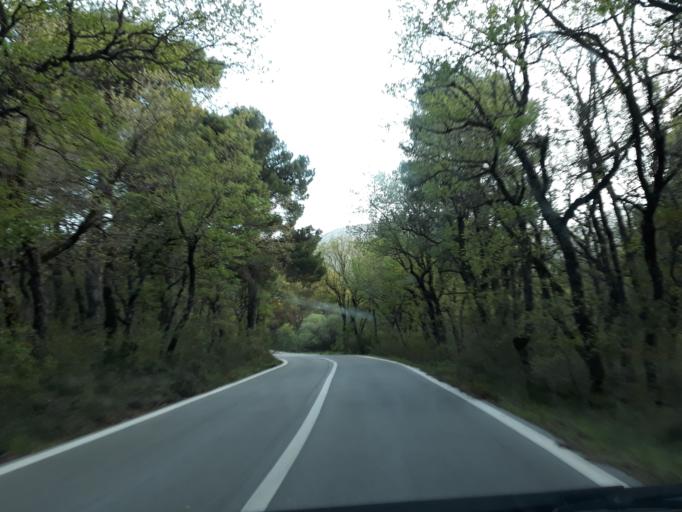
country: GR
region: Attica
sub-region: Nomarchia Anatolikis Attikis
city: Afidnes
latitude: 38.1990
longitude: 23.7857
